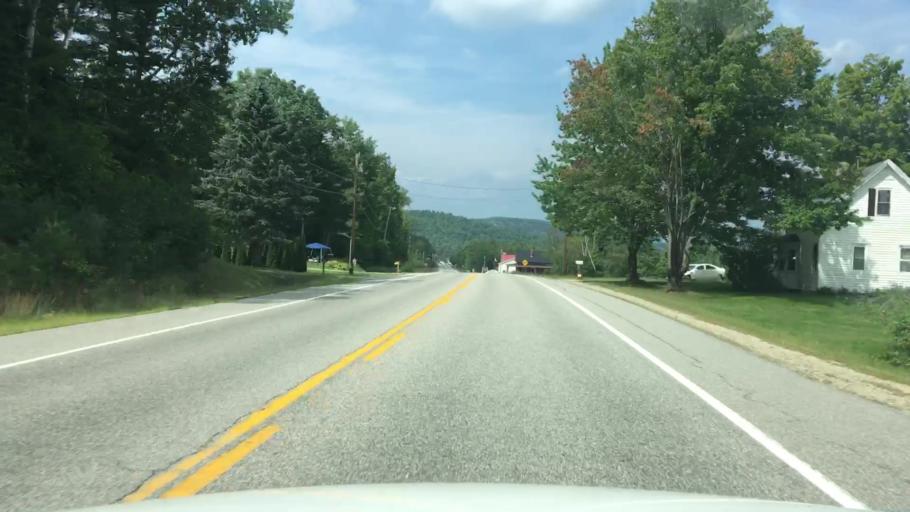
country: US
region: Maine
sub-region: Oxford County
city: Canton
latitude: 44.4339
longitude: -70.3050
